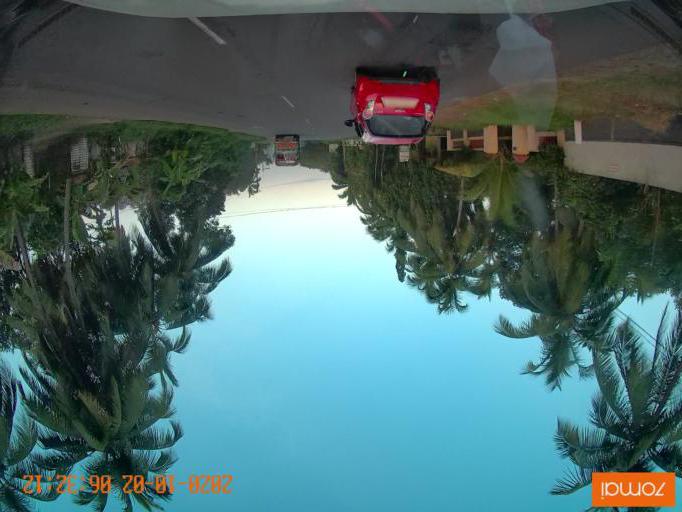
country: IN
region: Kerala
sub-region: Malappuram
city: Ponnani
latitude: 10.7491
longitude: 76.0235
